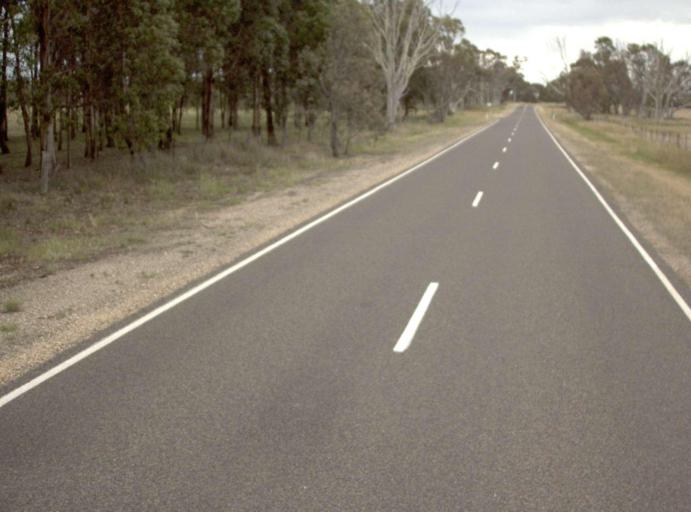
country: AU
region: Victoria
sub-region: East Gippsland
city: Bairnsdale
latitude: -37.9674
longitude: 147.4812
